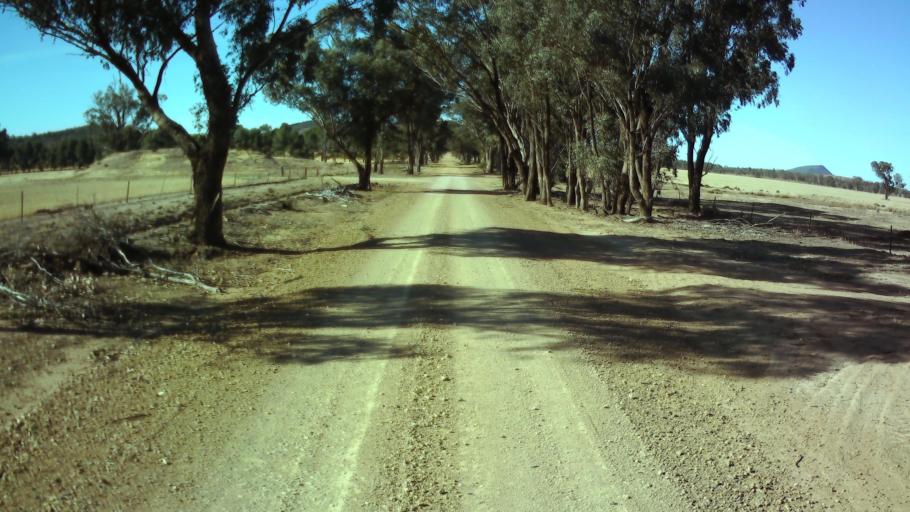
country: AU
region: New South Wales
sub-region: Weddin
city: Grenfell
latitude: -33.8089
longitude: 147.8776
